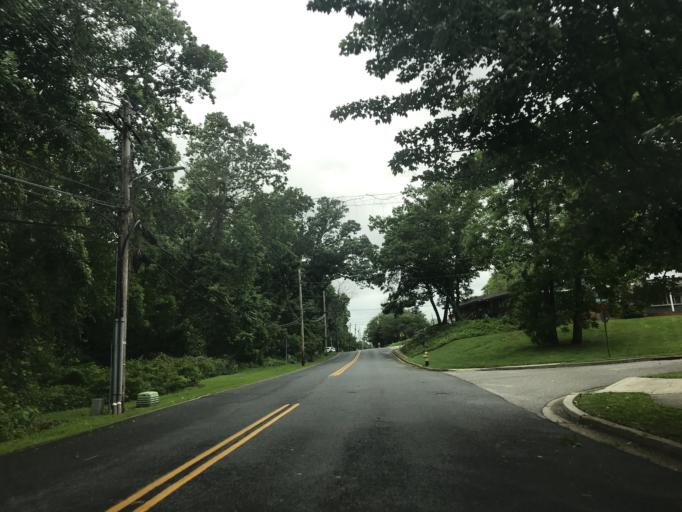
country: US
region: Maryland
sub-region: Anne Arundel County
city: Linthicum
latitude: 39.2092
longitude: -76.6541
